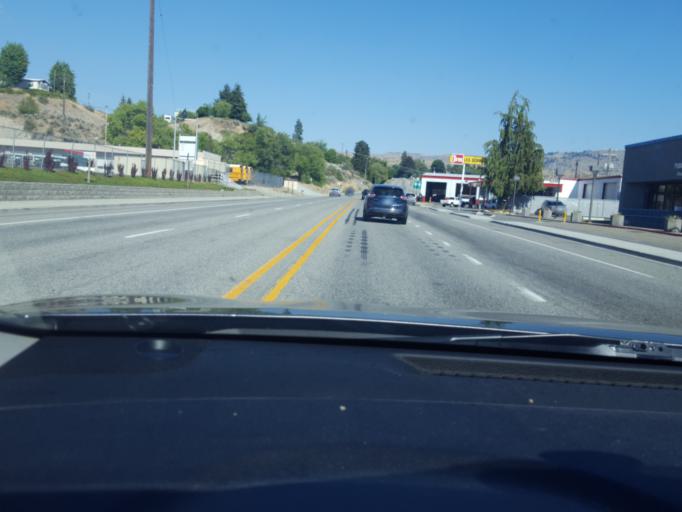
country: US
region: Washington
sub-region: Chelan County
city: Chelan
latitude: 47.8395
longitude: -120.0011
